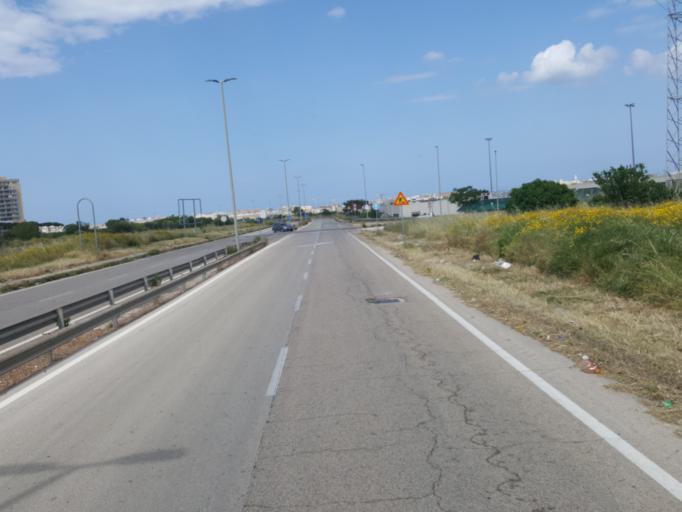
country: IT
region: Apulia
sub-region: Provincia di Bari
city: San Paolo
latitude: 41.1187
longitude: 16.8035
